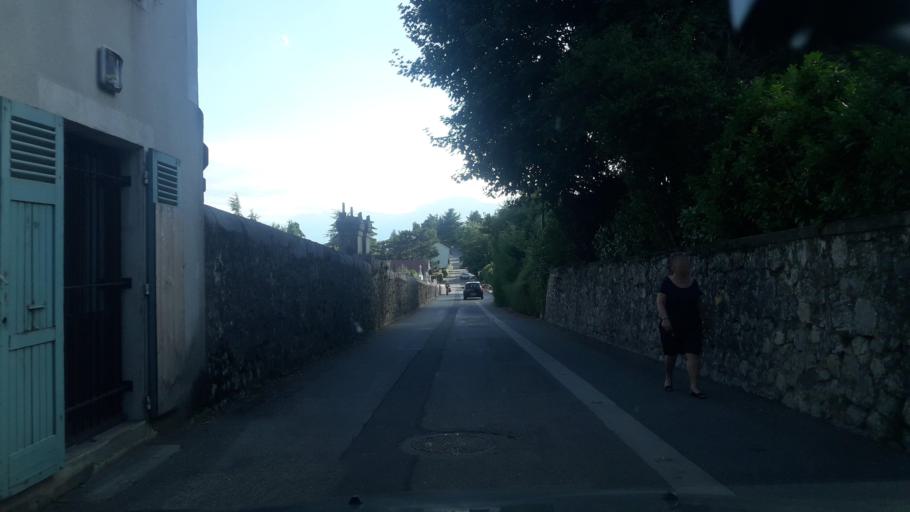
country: FR
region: Rhone-Alpes
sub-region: Departement de l'Isere
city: Saint-Ismier
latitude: 45.2481
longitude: 5.8257
